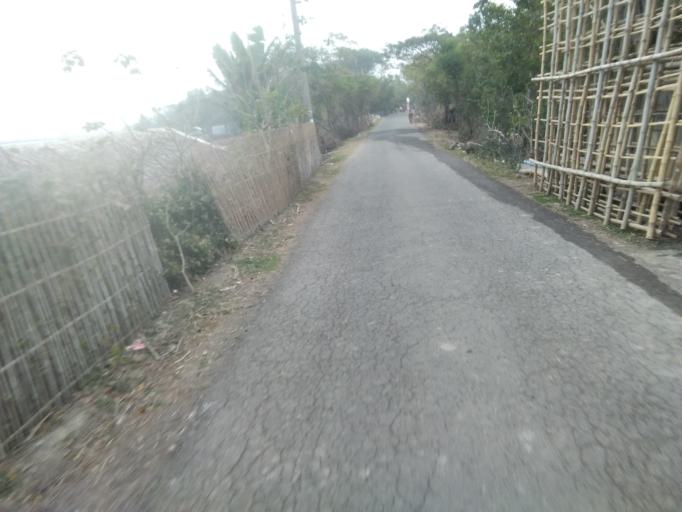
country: BD
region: Khulna
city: Satkhira
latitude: 22.5764
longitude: 89.0740
